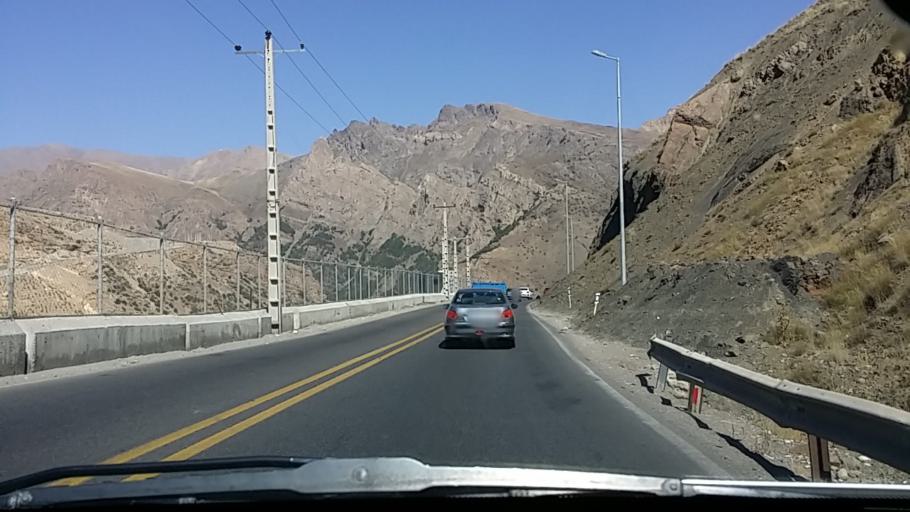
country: IR
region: Tehran
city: Tajrish
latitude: 36.1962
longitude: 51.3215
